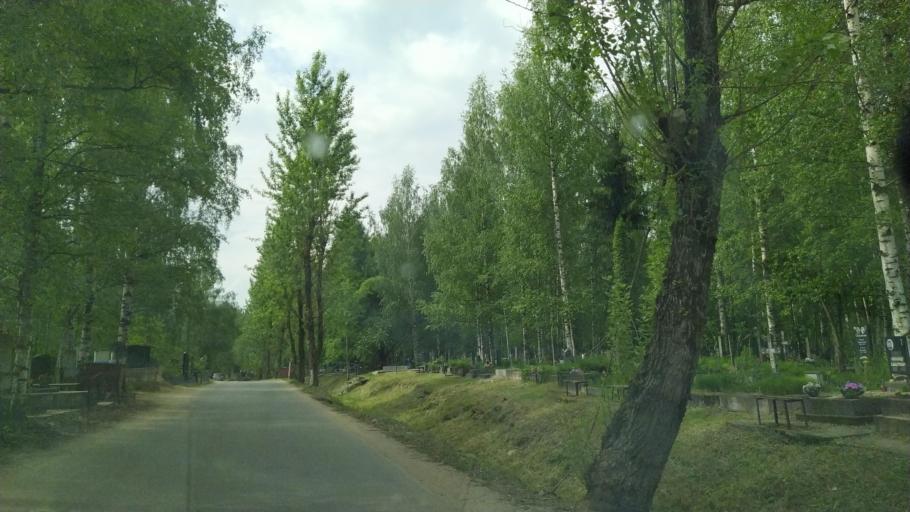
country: RU
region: St.-Petersburg
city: Dachnoye
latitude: 59.7663
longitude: 30.2623
